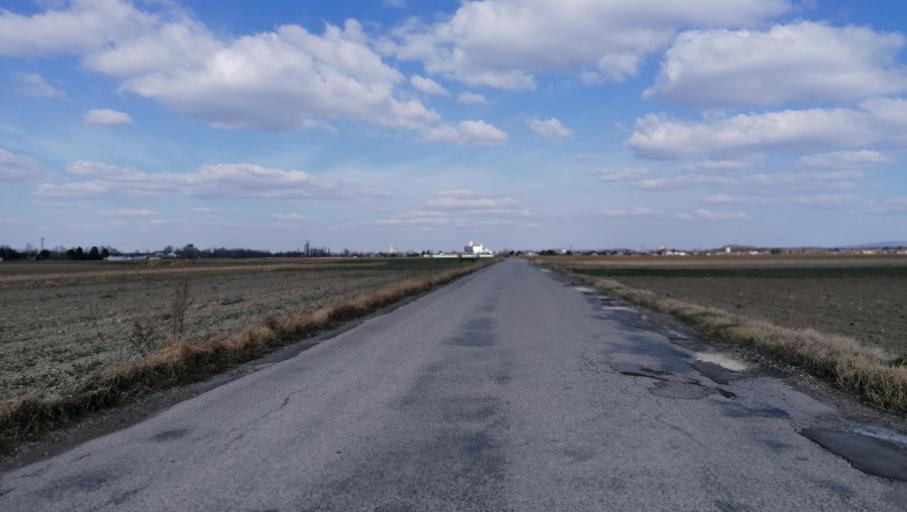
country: AT
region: Lower Austria
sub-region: Politischer Bezirk Wiener Neustadt
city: Lichtenworth
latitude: 47.8195
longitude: 16.2721
